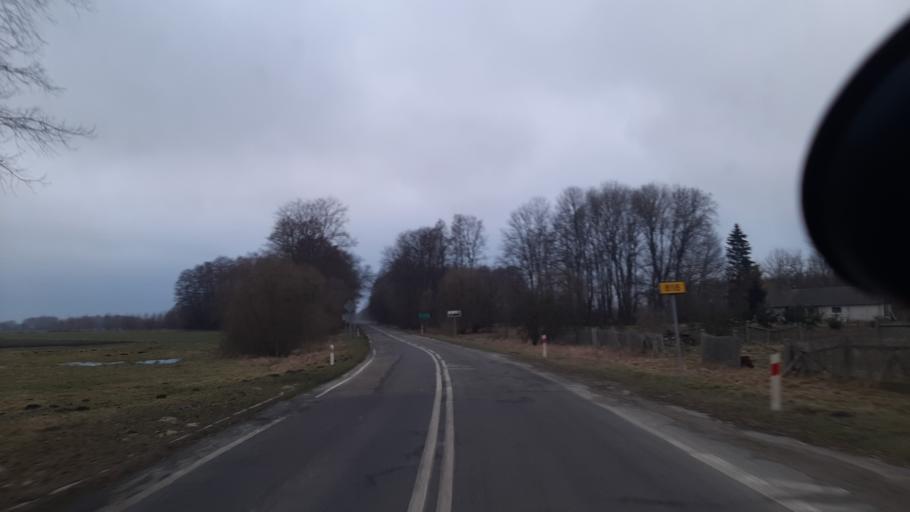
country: PL
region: Lublin Voivodeship
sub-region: Powiat parczewski
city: Sosnowica
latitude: 51.6133
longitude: 23.1211
